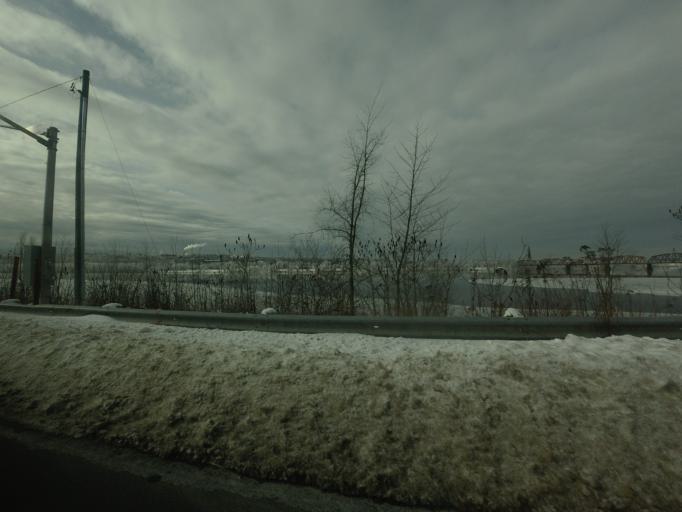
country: CA
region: New Brunswick
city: Fredericton
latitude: 45.9537
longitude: -66.6233
